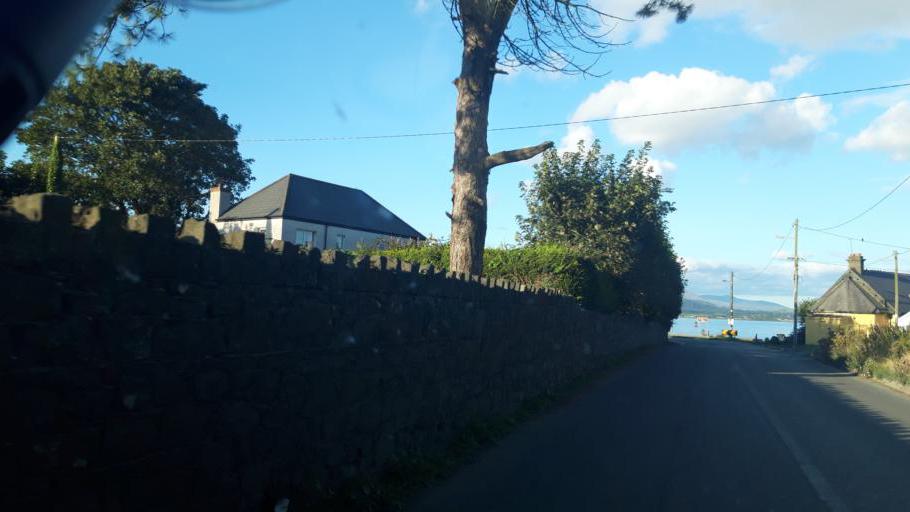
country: IE
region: Leinster
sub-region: Lu
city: Carlingford
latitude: 54.0313
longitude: -6.1317
